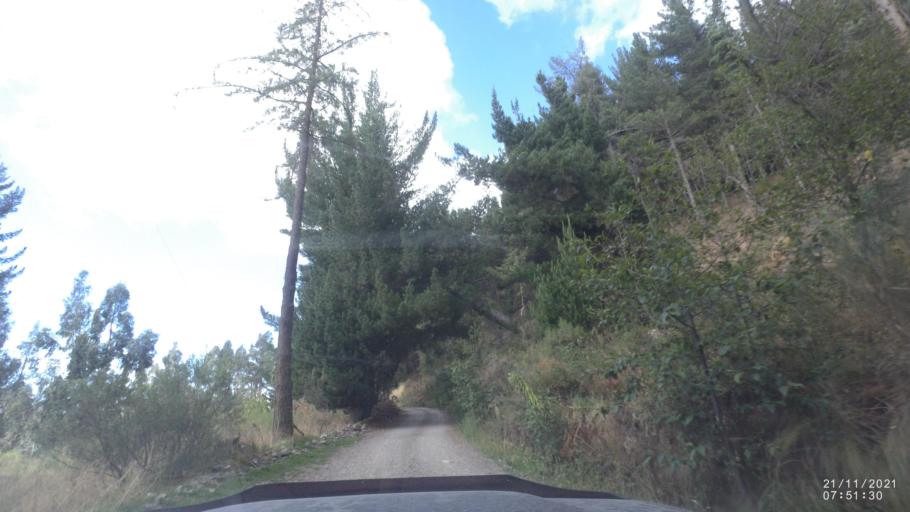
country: BO
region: Cochabamba
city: Cochabamba
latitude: -17.3053
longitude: -66.2166
